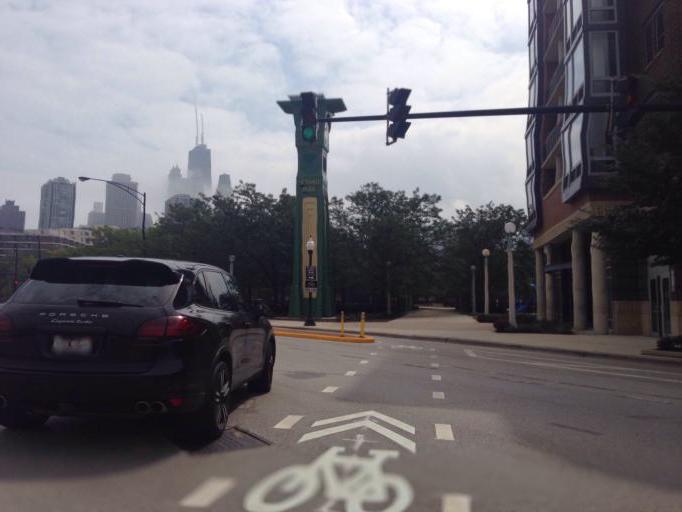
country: US
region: Illinois
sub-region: Cook County
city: Chicago
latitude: 41.9038
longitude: -87.6398
